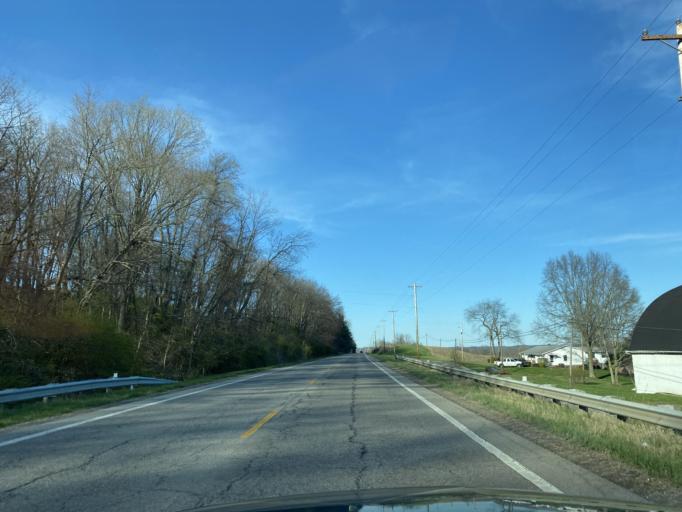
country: US
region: Ohio
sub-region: Wayne County
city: Shreve
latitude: 40.7073
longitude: -82.0133
